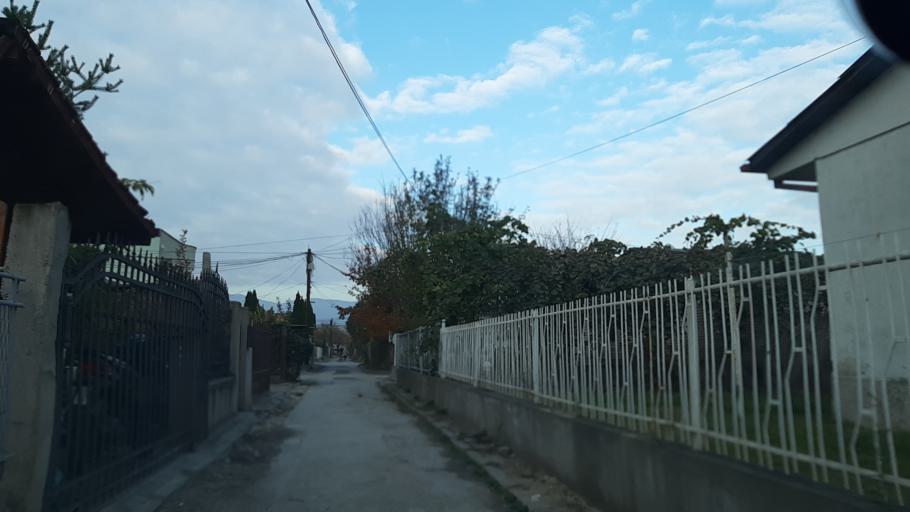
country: MK
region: Kisela Voda
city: Usje
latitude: 41.9738
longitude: 21.4575
